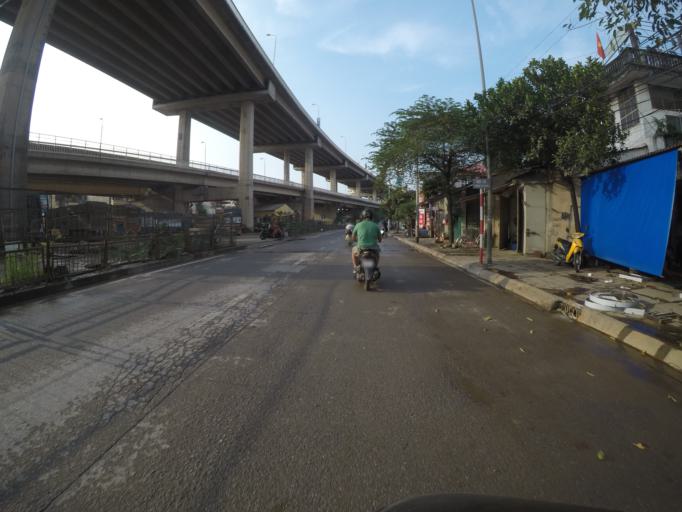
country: VN
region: Ha Noi
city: Tay Ho
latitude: 21.0893
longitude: 105.7862
